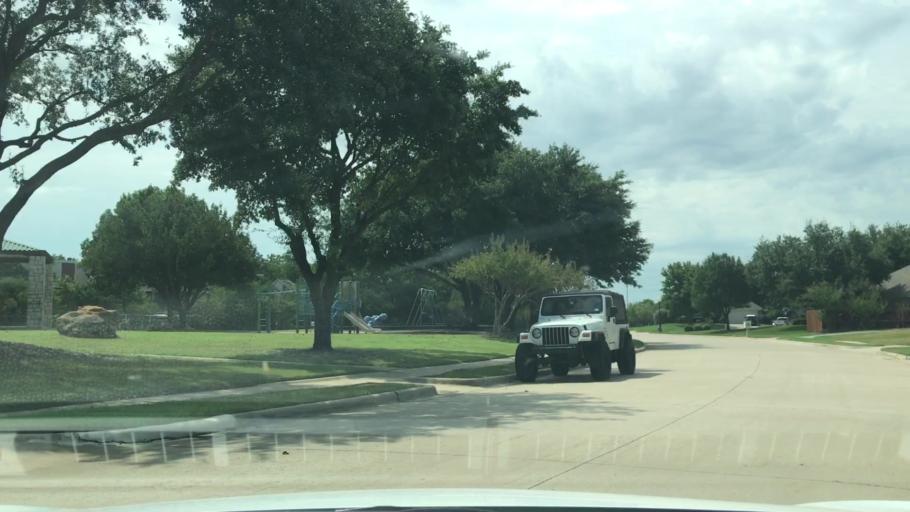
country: US
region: Texas
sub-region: Tarrant County
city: Euless
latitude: 32.8535
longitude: -97.0777
